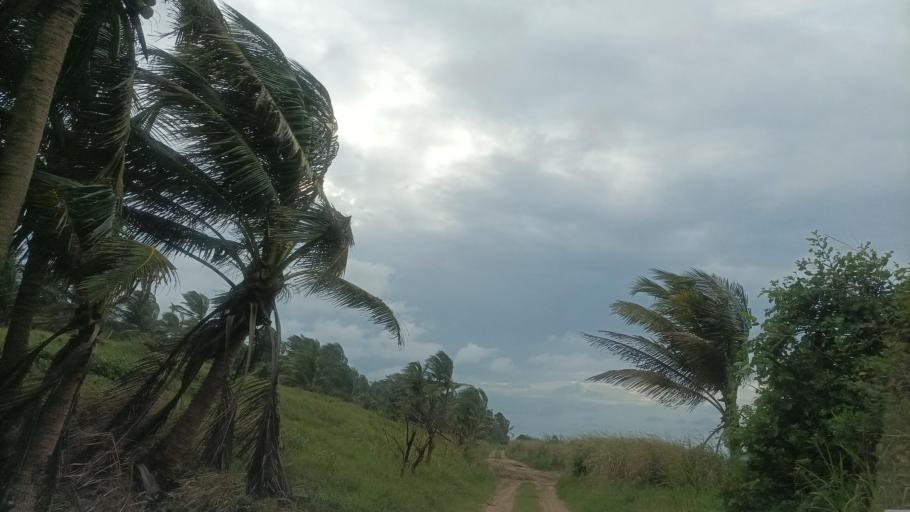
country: MX
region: Veracruz
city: Agua Dulce
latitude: 18.1820
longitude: -94.2636
